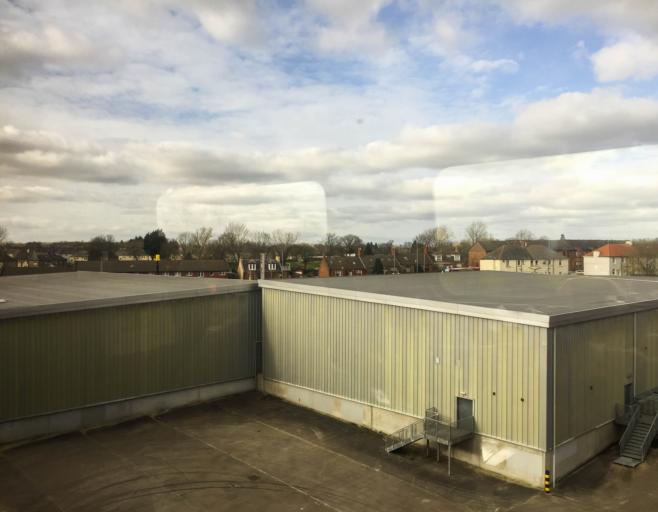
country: GB
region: Scotland
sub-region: North Lanarkshire
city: Wishaw
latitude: 55.7743
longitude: -3.9318
